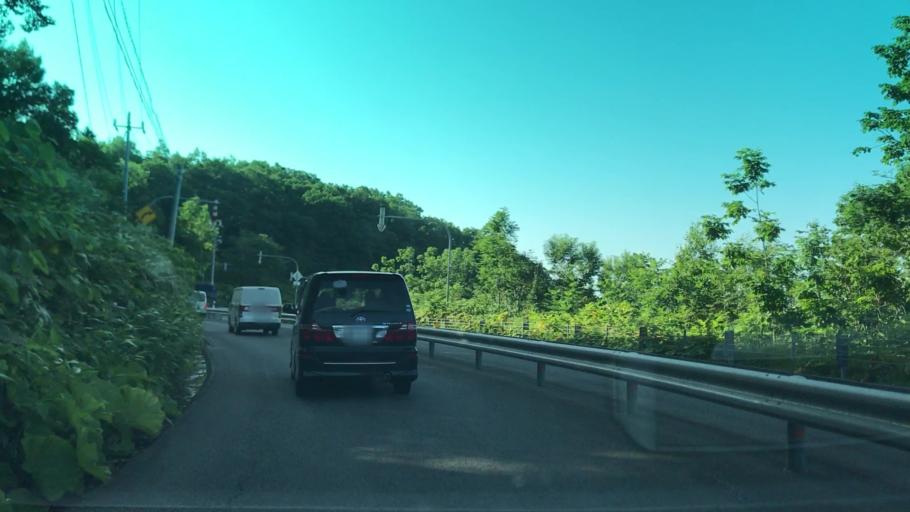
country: JP
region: Hokkaido
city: Otaru
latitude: 43.1421
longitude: 141.0129
